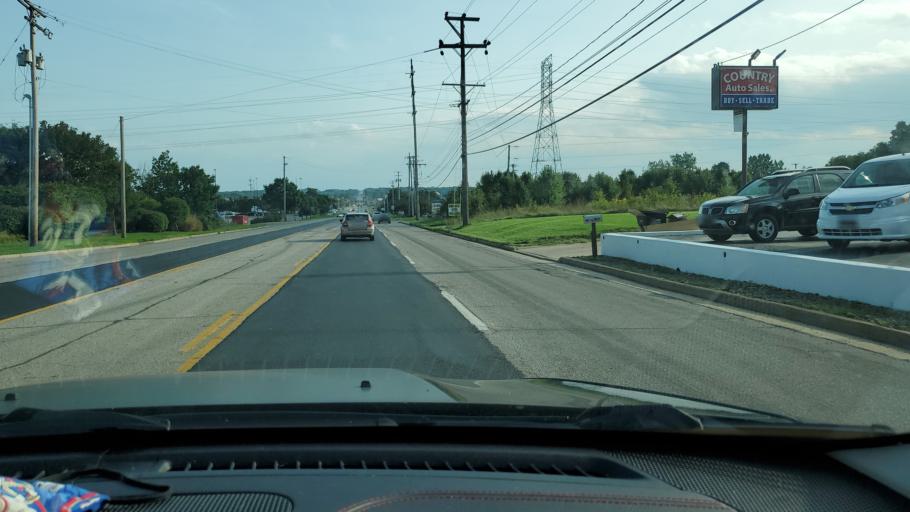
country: US
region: Ohio
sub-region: Mahoning County
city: Poland
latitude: 41.0335
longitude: -80.6347
